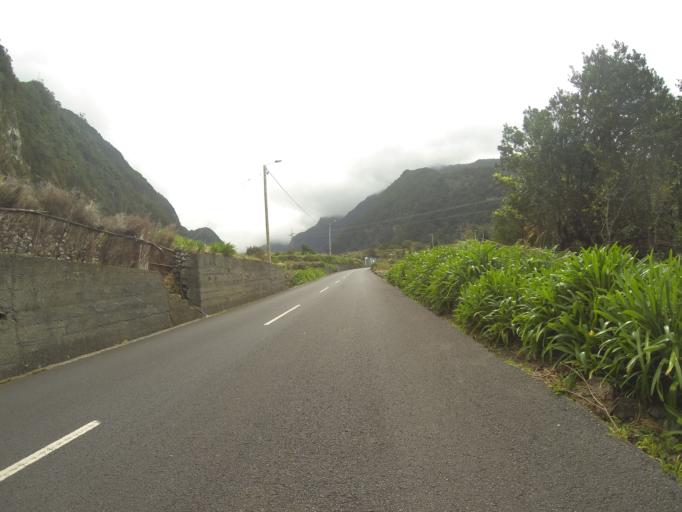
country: PT
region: Madeira
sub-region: Porto Moniz
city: Porto Moniz
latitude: 32.8203
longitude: -17.1086
